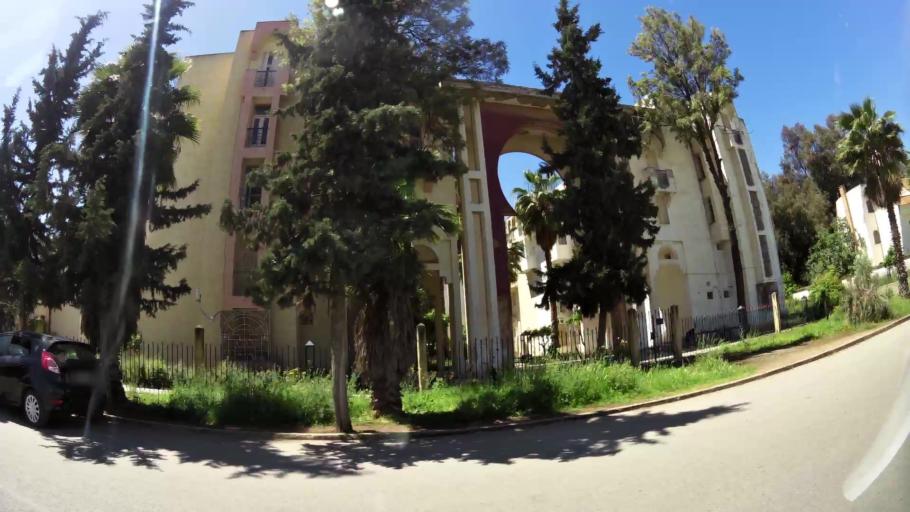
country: MA
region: Meknes-Tafilalet
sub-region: Meknes
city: Meknes
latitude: 33.9003
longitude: -5.5295
